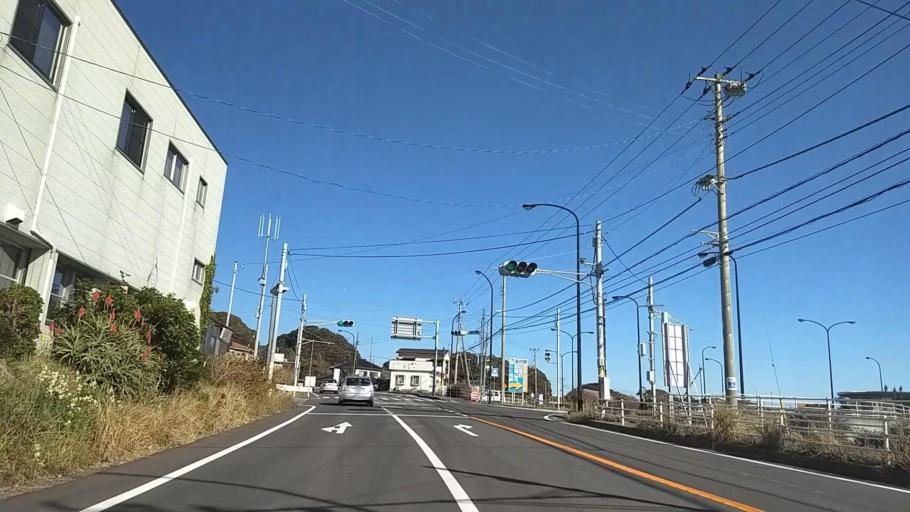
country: JP
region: Chiba
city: Kawaguchi
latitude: 35.0643
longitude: 140.0764
